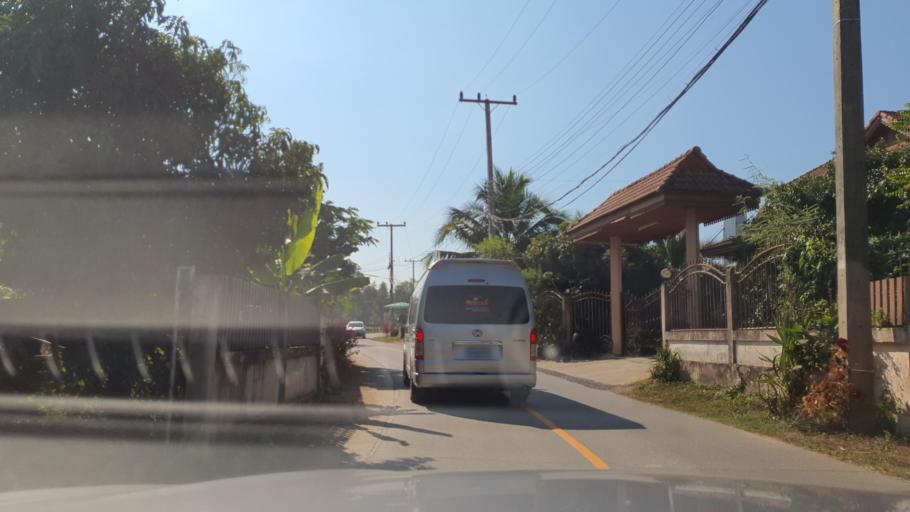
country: TH
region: Nan
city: Pua
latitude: 19.1634
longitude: 100.9292
